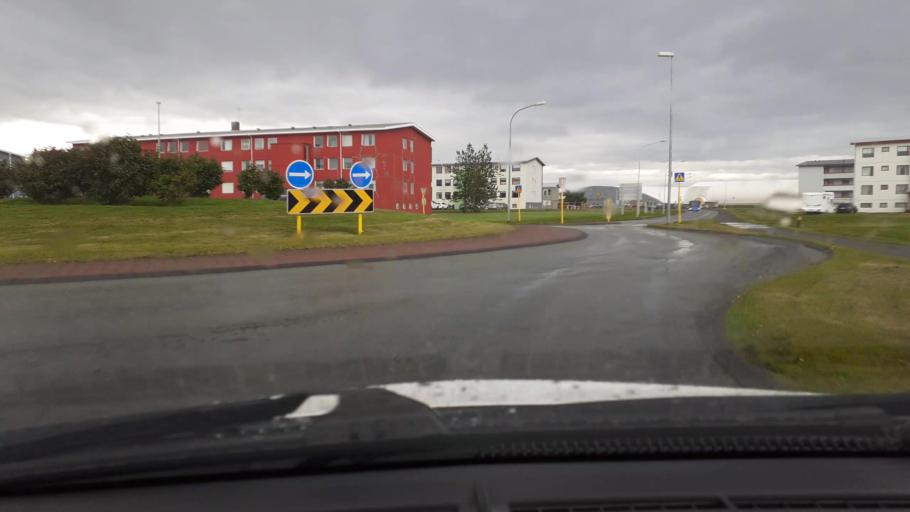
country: IS
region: West
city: Akranes
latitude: 64.3213
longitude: -22.0599
